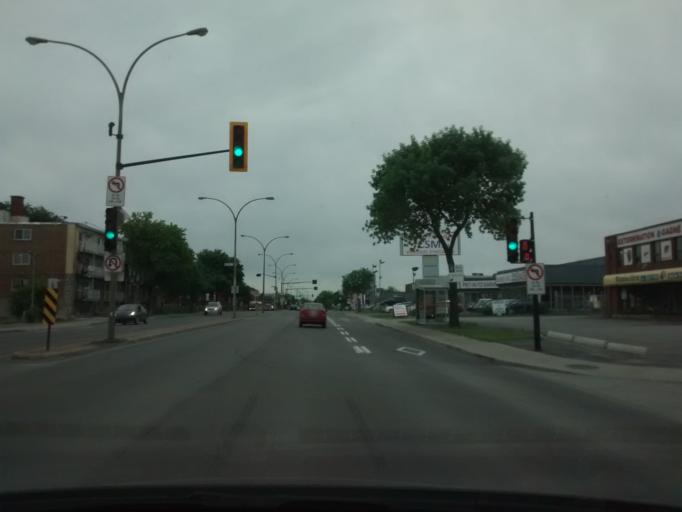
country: CA
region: Quebec
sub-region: Montreal
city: Saint-Leonard
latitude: 45.5828
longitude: -73.6284
